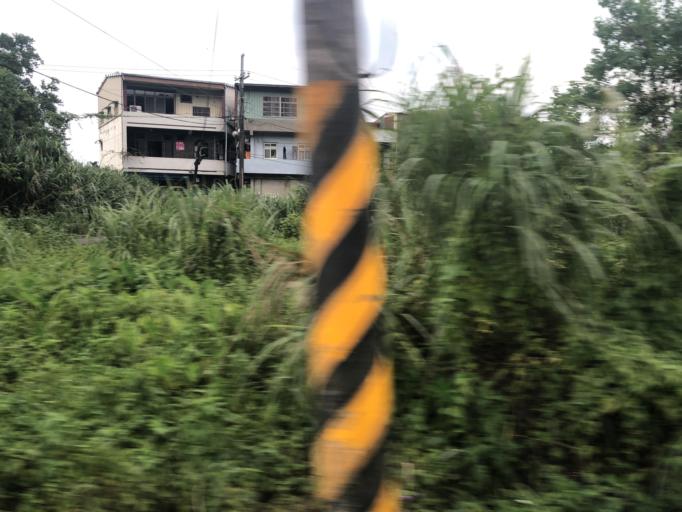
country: TW
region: Taiwan
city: Daxi
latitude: 24.9156
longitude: 121.3627
